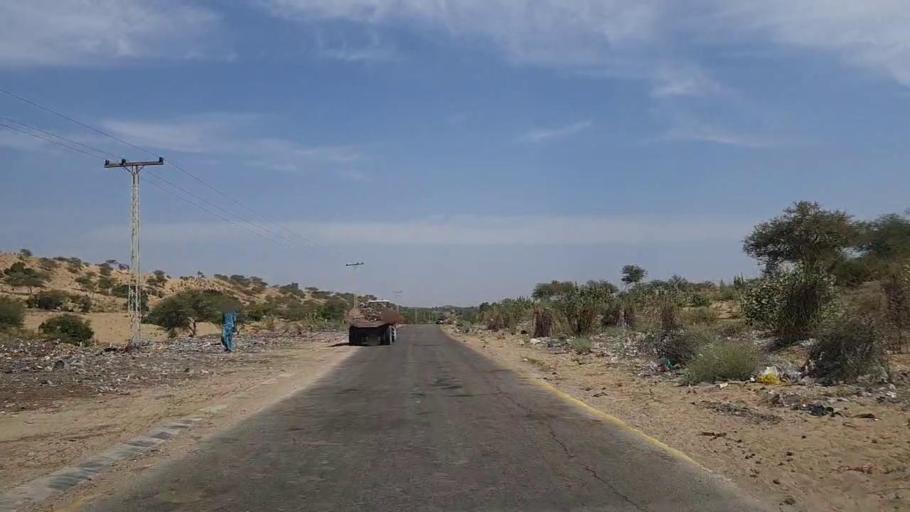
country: PK
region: Sindh
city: Mithi
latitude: 24.7739
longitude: 69.8031
